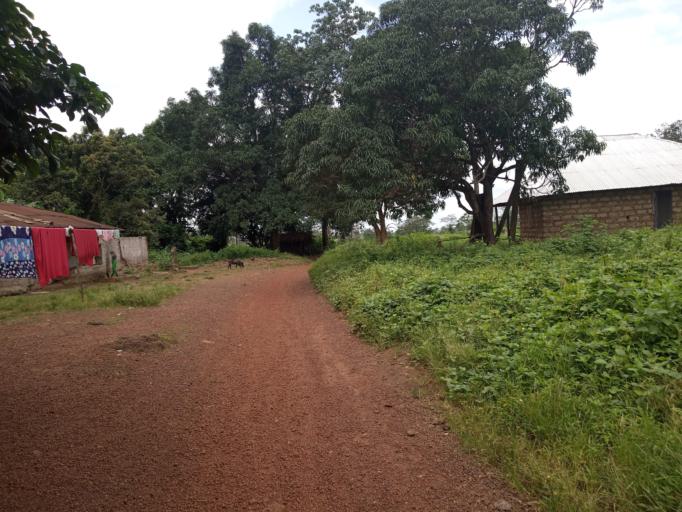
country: SL
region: Northern Province
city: Kamakwie
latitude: 9.4811
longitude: -12.2536
